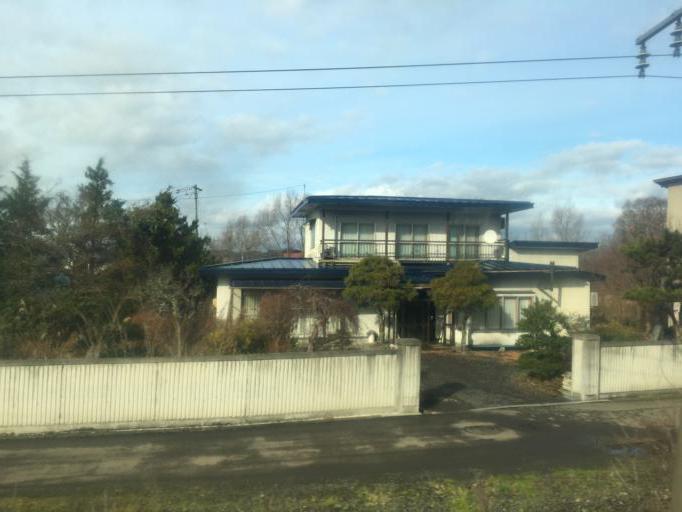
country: JP
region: Akita
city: Takanosu
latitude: 40.2364
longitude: 140.3807
